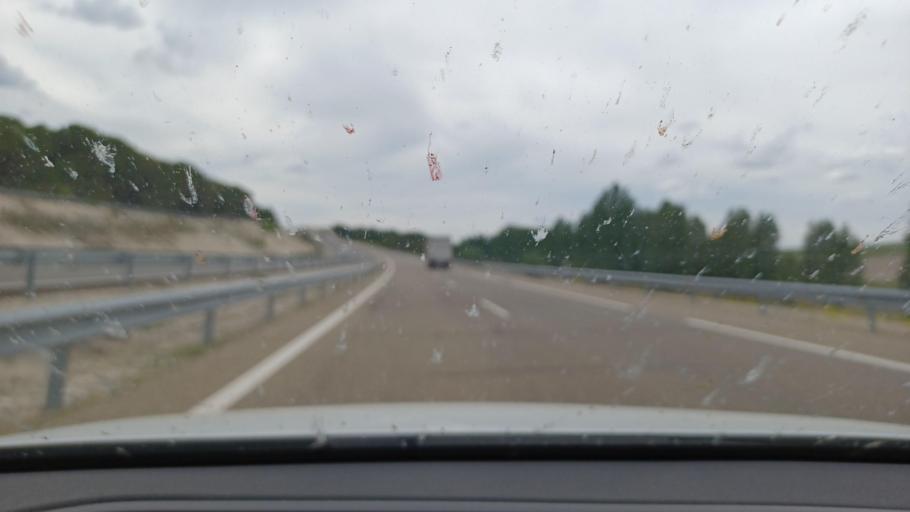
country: ES
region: Castille and Leon
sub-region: Provincia de Valladolid
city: Viloria
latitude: 41.4426
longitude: -4.4123
